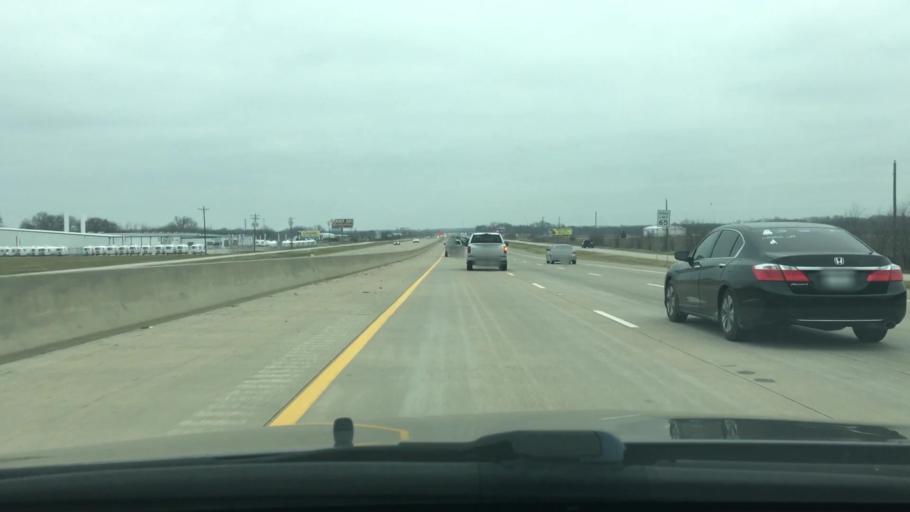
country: US
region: Texas
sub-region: Navarro County
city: Corsicana
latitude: 32.1930
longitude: -96.4730
